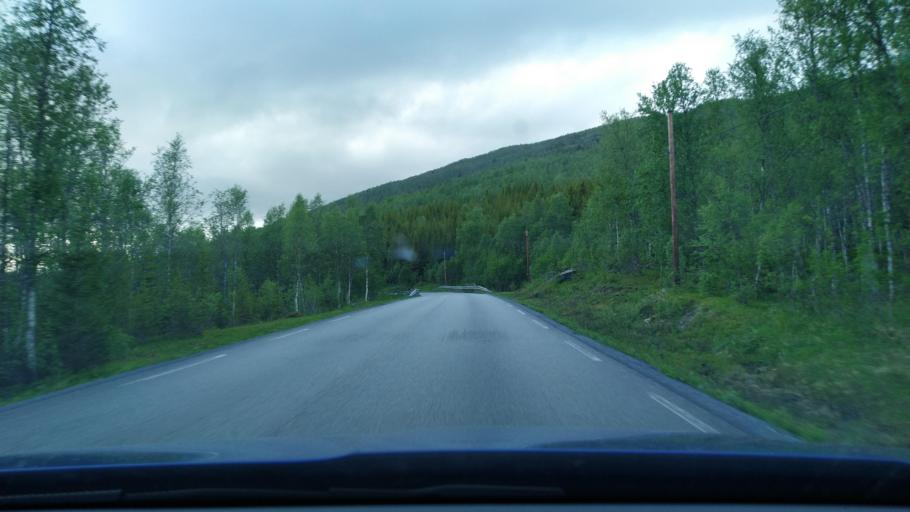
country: NO
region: Troms
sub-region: Dyroy
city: Brostadbotn
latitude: 69.0536
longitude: 17.8185
